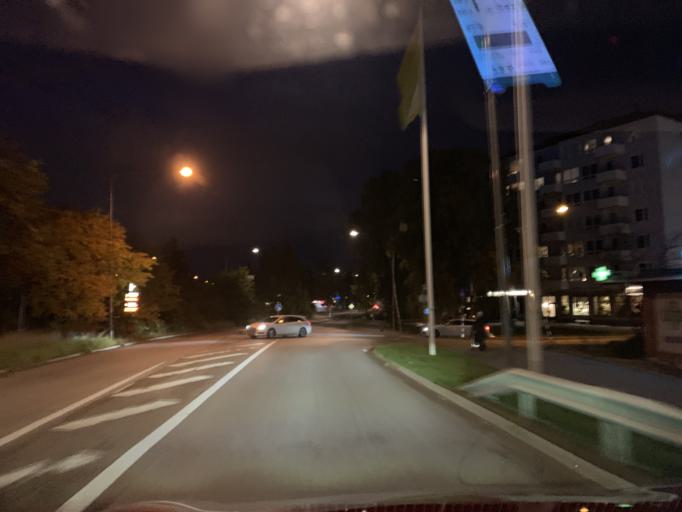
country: SE
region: Stockholm
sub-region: Huddinge Kommun
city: Huddinge
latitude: 59.2371
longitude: 17.9807
